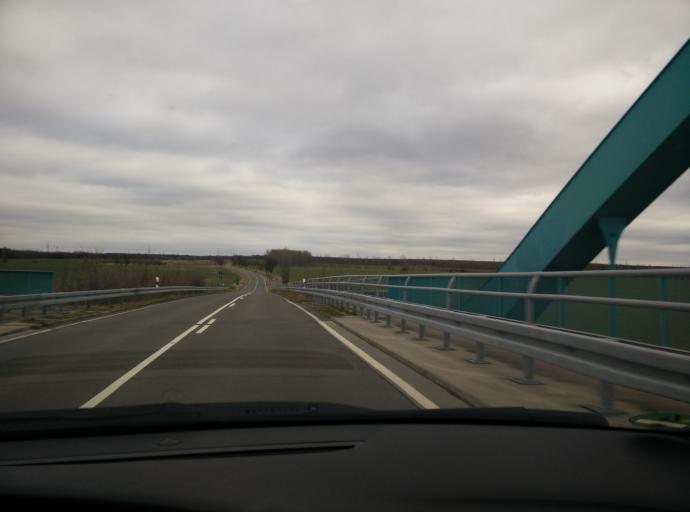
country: DE
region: Saxony
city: Borna
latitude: 51.1306
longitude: 12.5165
